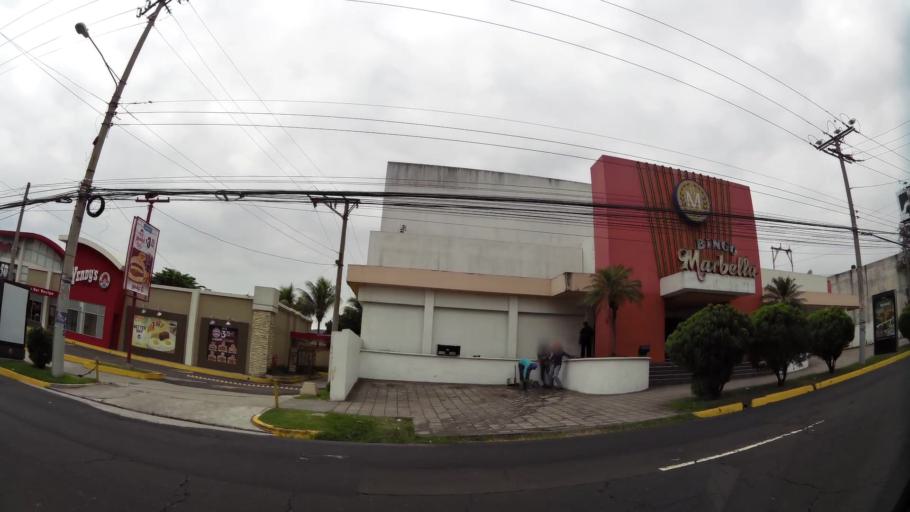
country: SV
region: San Salvador
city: Mejicanos
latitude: 13.7021
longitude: -89.2316
